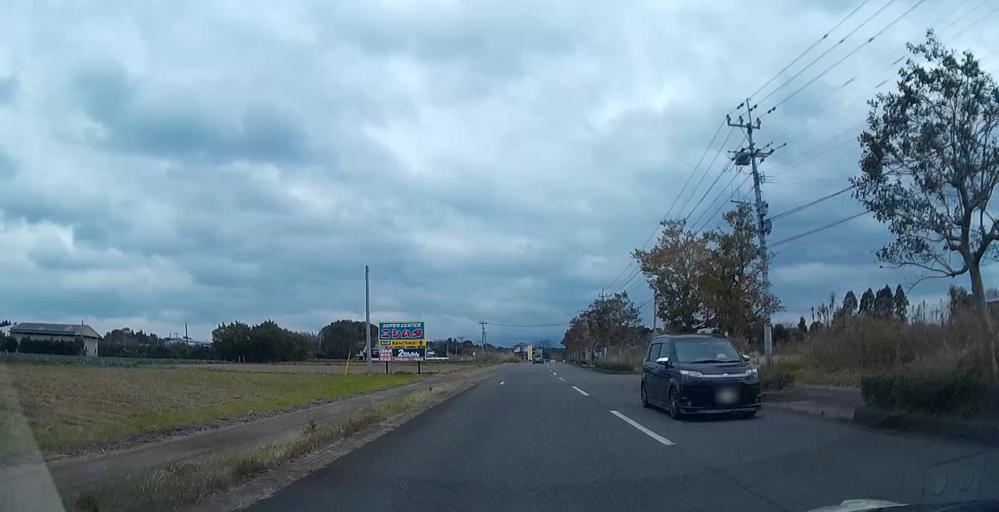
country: JP
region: Kagoshima
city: Akune
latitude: 32.0750
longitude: 130.2113
